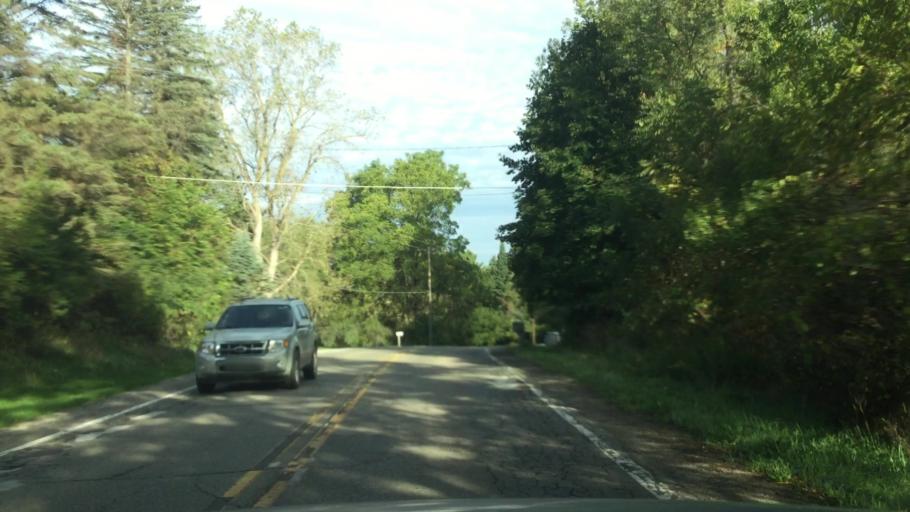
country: US
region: Michigan
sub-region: Livingston County
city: Brighton
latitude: 42.4842
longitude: -83.8506
